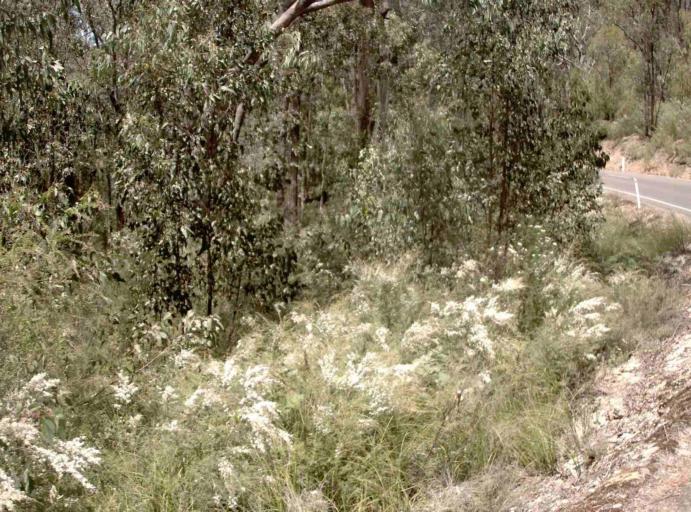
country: AU
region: Victoria
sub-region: East Gippsland
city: Lakes Entrance
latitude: -37.5786
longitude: 147.8946
